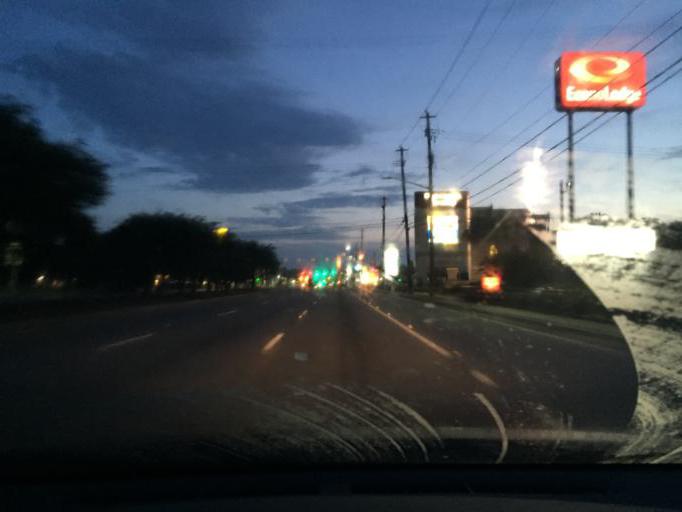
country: US
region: Georgia
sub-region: Chatham County
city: Isle of Hope
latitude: 32.0081
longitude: -81.1151
